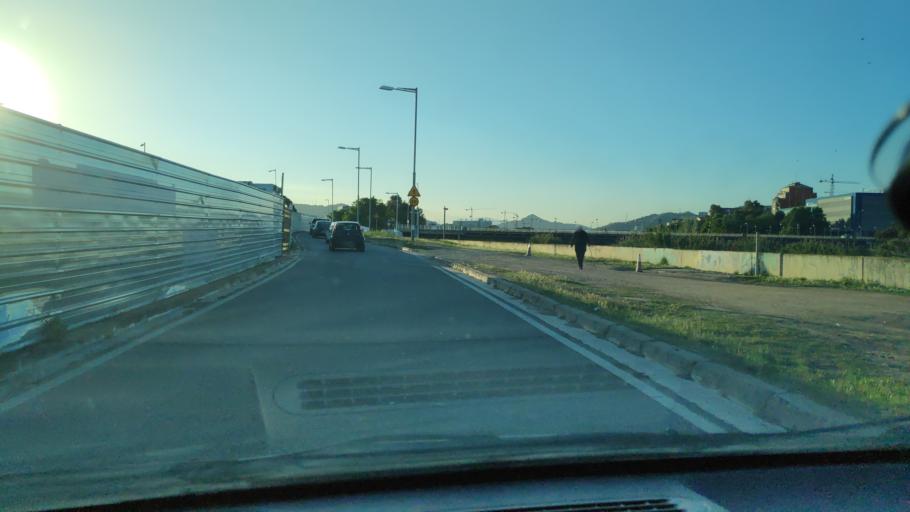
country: ES
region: Catalonia
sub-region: Provincia de Barcelona
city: Sant Adria de Besos
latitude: 41.4291
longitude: 2.2148
